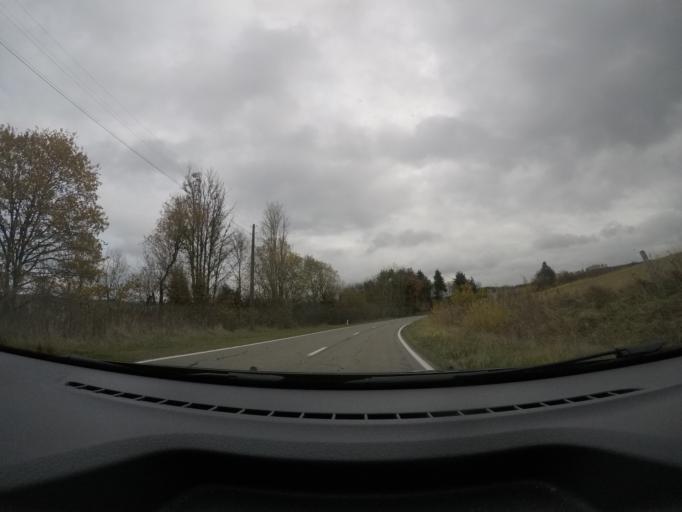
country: BE
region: Wallonia
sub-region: Province du Luxembourg
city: Houffalize
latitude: 50.1482
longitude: 5.7155
